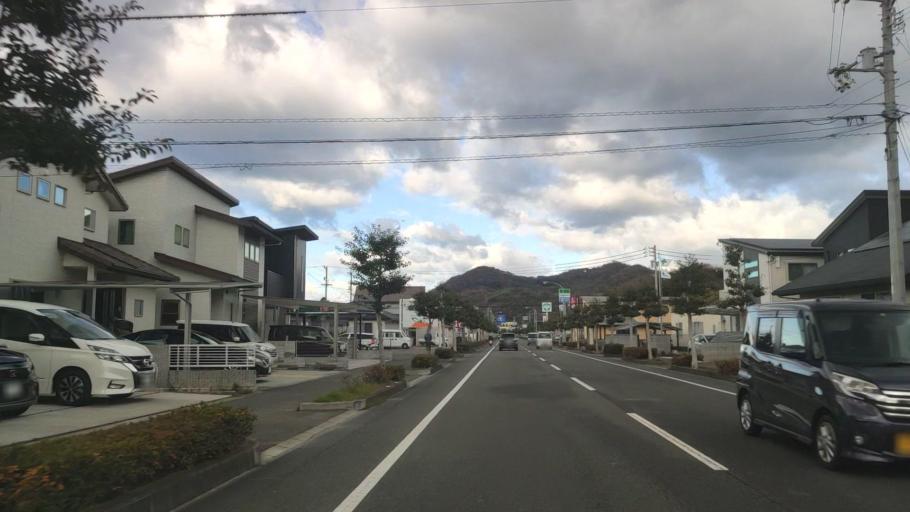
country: JP
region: Ehime
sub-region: Shikoku-chuo Shi
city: Matsuyama
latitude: 33.8689
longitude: 132.7236
